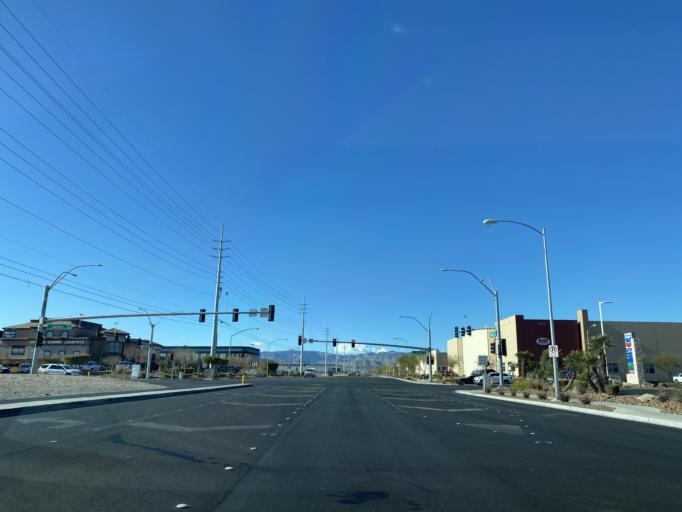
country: US
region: Nevada
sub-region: Clark County
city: Spring Valley
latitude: 36.0709
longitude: -115.2235
